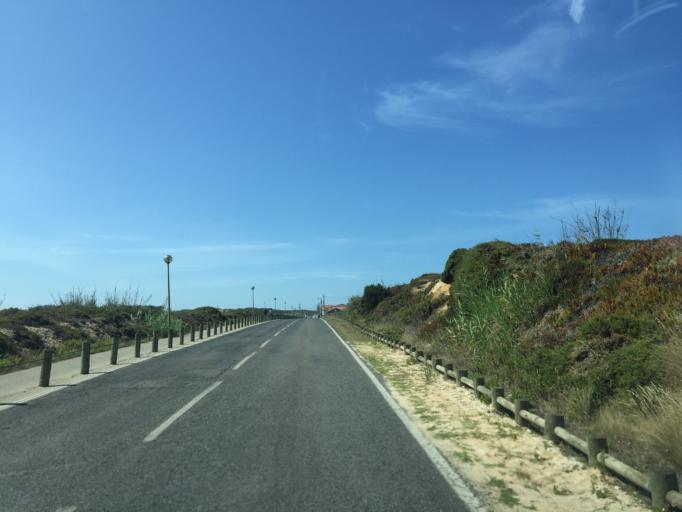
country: PT
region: Lisbon
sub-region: Torres Vedras
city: Silveira
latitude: 39.1658
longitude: -9.3591
